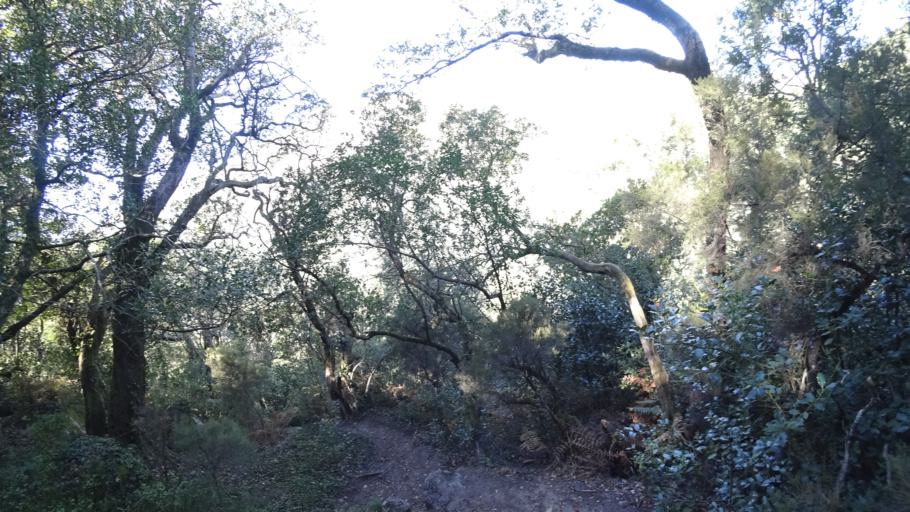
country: PT
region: Braga
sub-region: Vieira do Minho
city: Real
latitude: 41.7561
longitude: -8.1474
